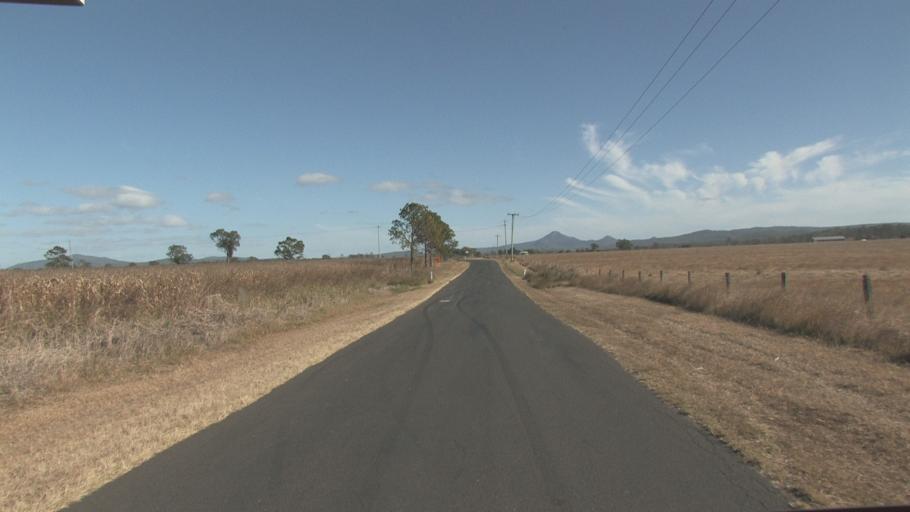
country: AU
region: Queensland
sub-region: Logan
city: Cedar Vale
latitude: -27.8532
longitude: 152.9625
